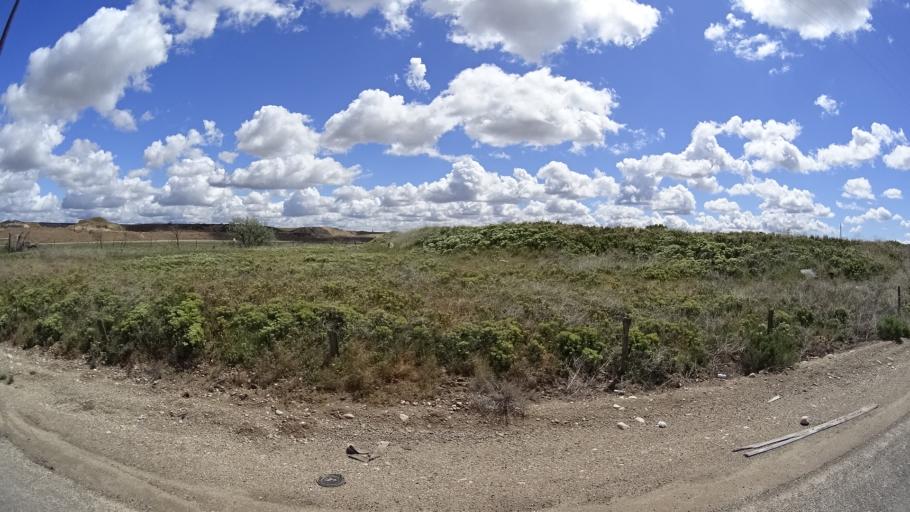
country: US
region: Idaho
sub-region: Ada County
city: Garden City
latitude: 43.4892
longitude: -116.2743
